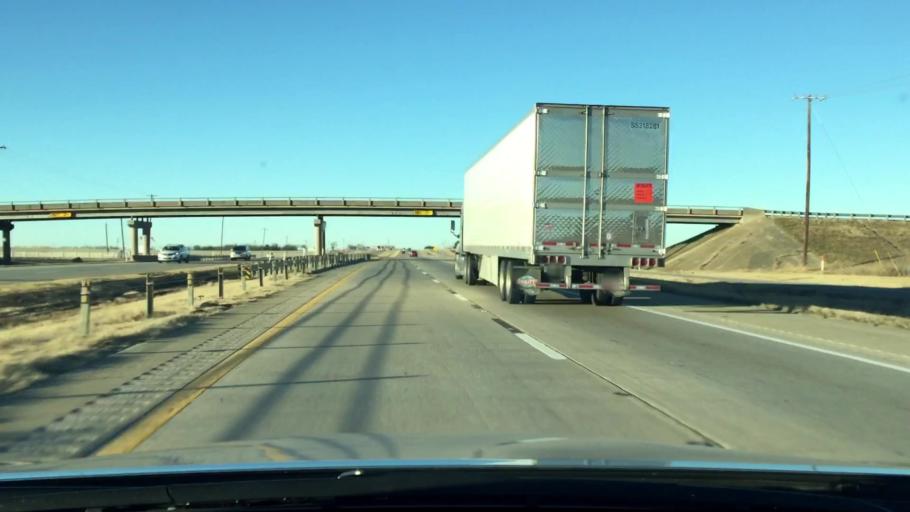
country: US
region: Texas
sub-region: Cooke County
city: Gainesville
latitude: 33.5168
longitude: -97.1661
